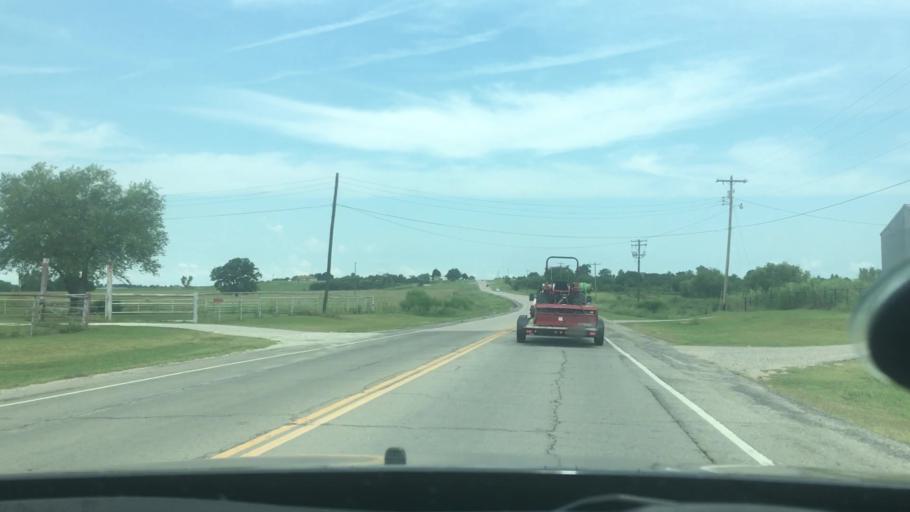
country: US
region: Oklahoma
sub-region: Seminole County
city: Seminole
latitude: 35.2690
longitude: -96.7187
